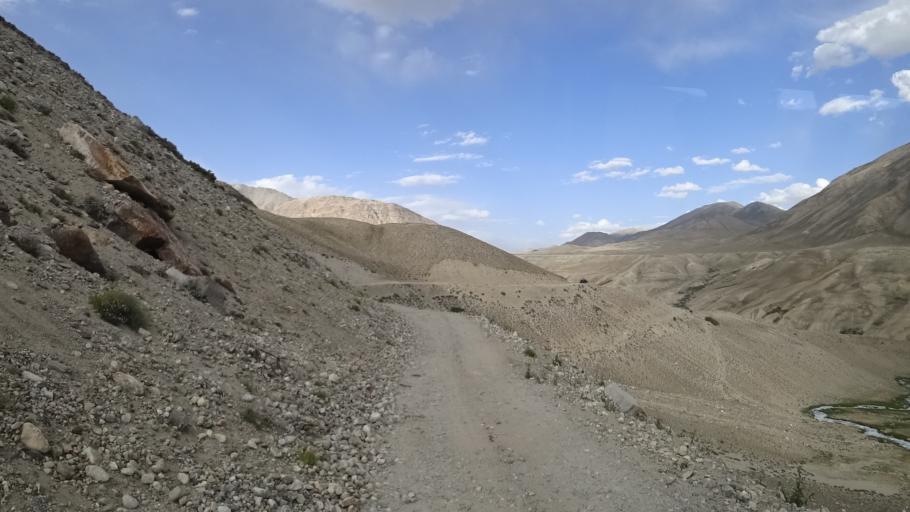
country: AF
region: Badakhshan
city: Khandud
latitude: 37.2215
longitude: 72.7899
